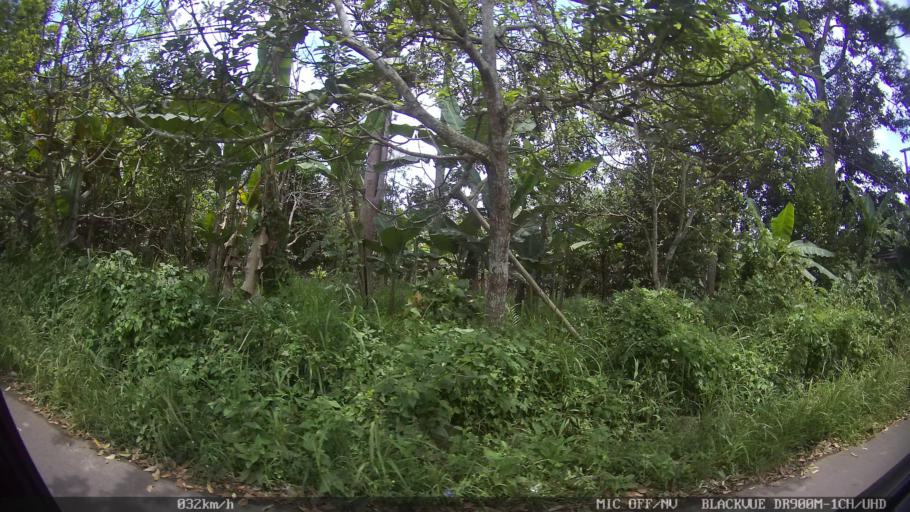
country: ID
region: Lampung
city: Bandarlampung
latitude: -5.4207
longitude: 105.2239
